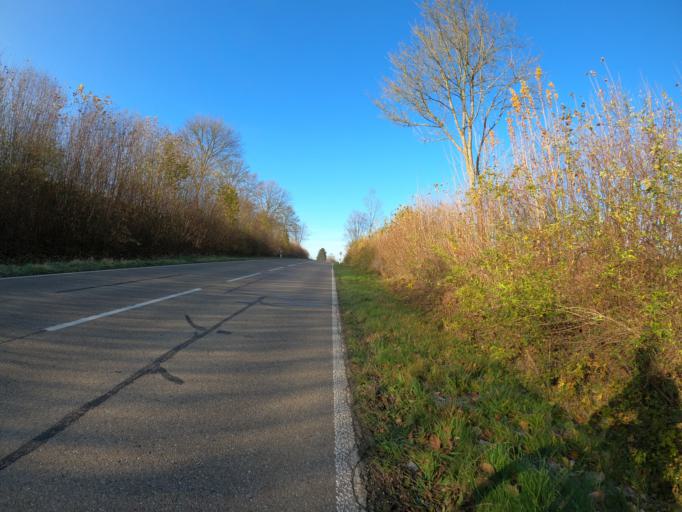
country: DE
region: Baden-Wuerttemberg
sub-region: Regierungsbezirk Stuttgart
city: Albershausen
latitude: 48.7065
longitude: 9.5647
